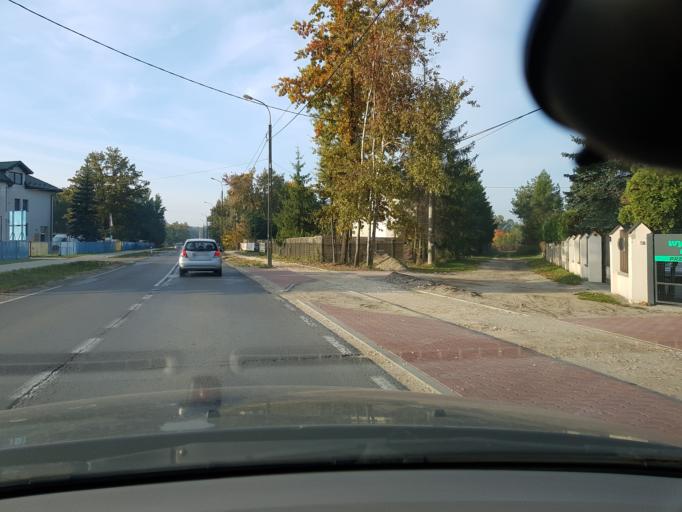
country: PL
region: Masovian Voivodeship
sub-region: Powiat minski
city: Halinow
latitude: 52.1814
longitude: 21.2998
